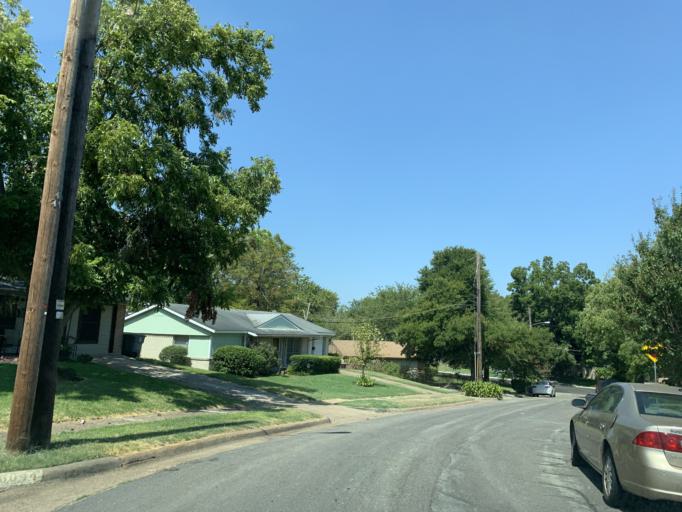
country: US
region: Texas
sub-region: Dallas County
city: Hutchins
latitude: 32.6747
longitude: -96.7539
